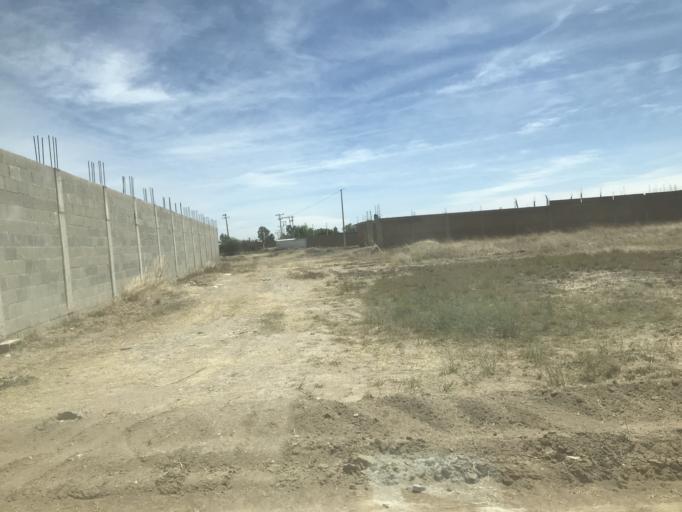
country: MX
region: Durango
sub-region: Durango
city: Sebastian Lerdo de Tejada
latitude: 23.9808
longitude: -104.6576
